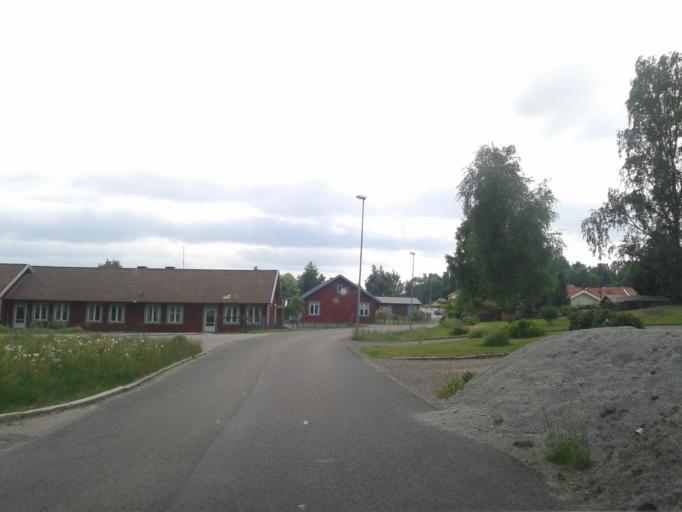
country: SE
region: Vaestra Goetaland
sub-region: Kungalvs Kommun
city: Kungalv
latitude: 57.8948
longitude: 11.9726
